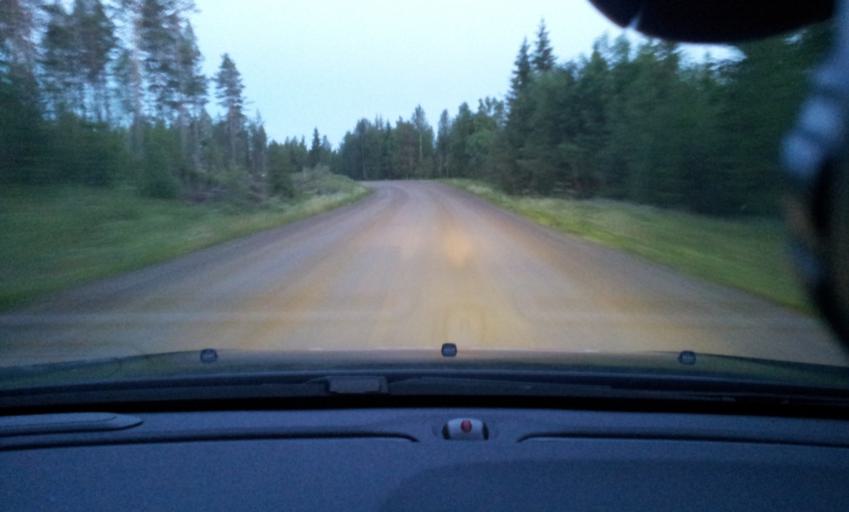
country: SE
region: Vaesternorrland
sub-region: Ange Kommun
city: Ange
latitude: 62.7414
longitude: 15.6413
